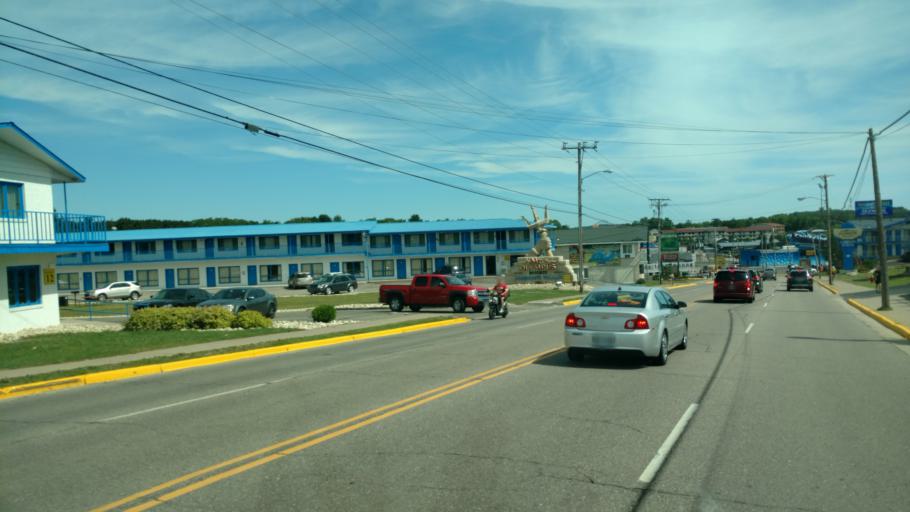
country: US
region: Wisconsin
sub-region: Sauk County
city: Lake Delton
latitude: 43.6027
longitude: -89.7925
